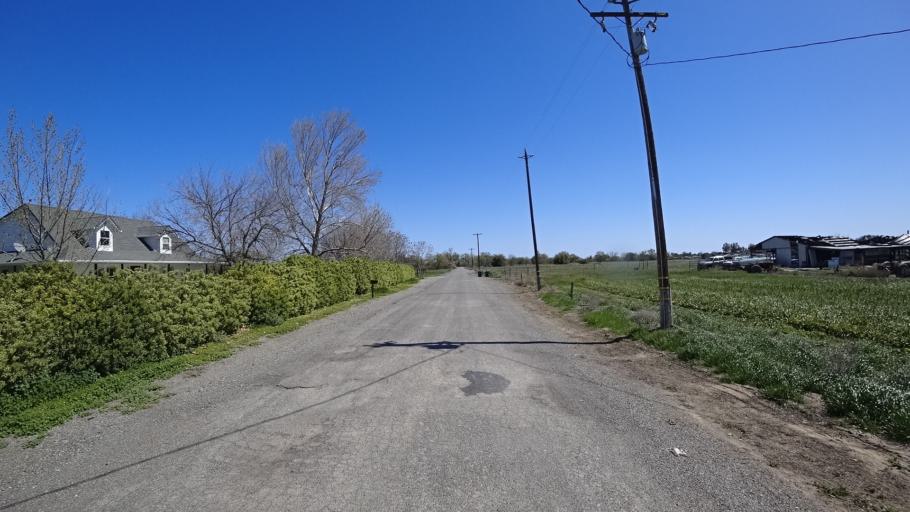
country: US
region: California
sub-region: Glenn County
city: Orland
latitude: 39.7841
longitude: -122.2447
